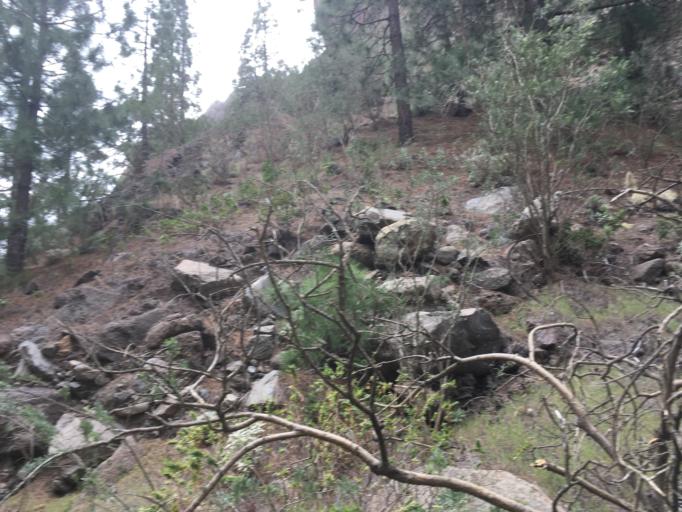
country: ES
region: Canary Islands
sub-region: Provincia de Santa Cruz de Tenerife
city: Vilaflor
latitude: 28.2011
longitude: -16.5771
